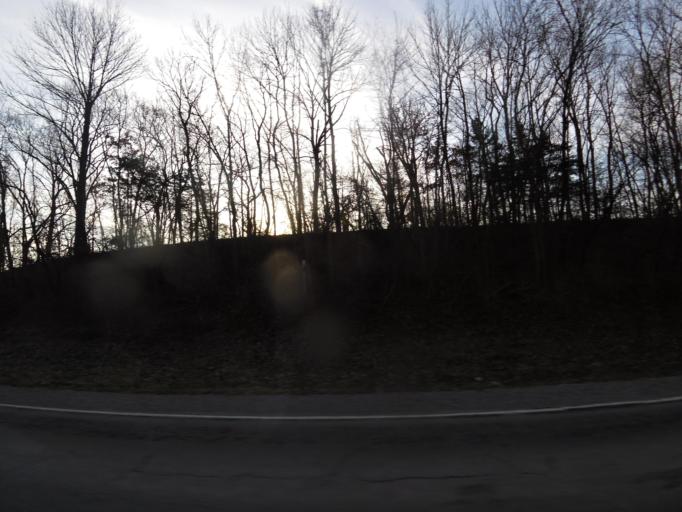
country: US
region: Illinois
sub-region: Bond County
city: Greenville
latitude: 38.9208
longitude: -89.2568
